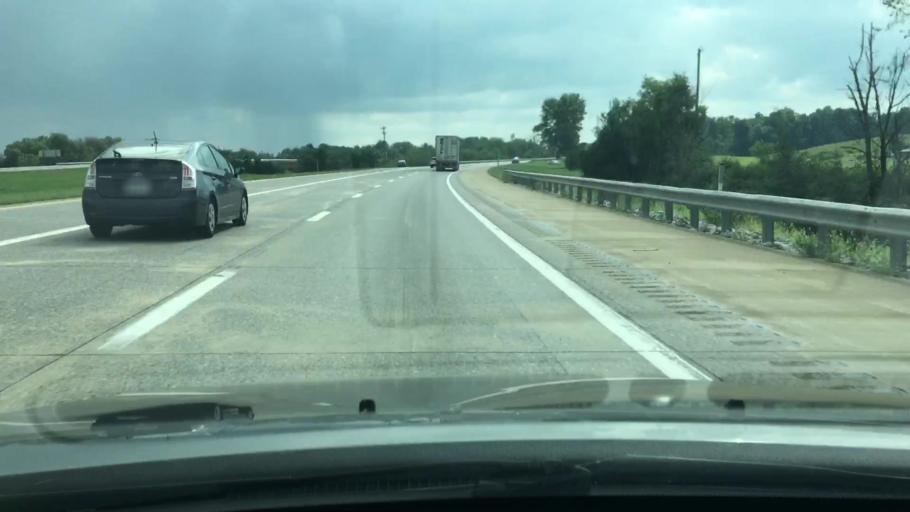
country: US
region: Pennsylvania
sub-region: Lebanon County
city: Jonestown
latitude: 40.4315
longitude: -76.5191
